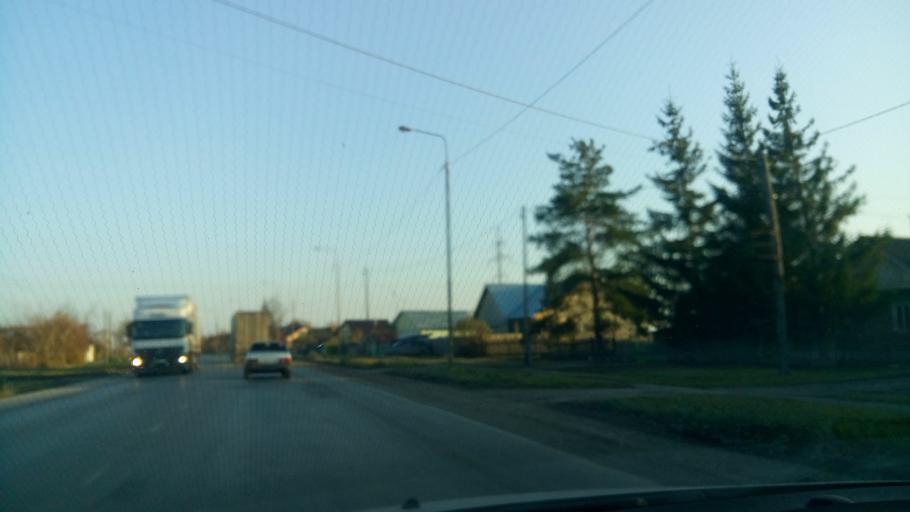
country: RU
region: Sverdlovsk
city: Bogdanovich
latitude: 56.7600
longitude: 62.0756
